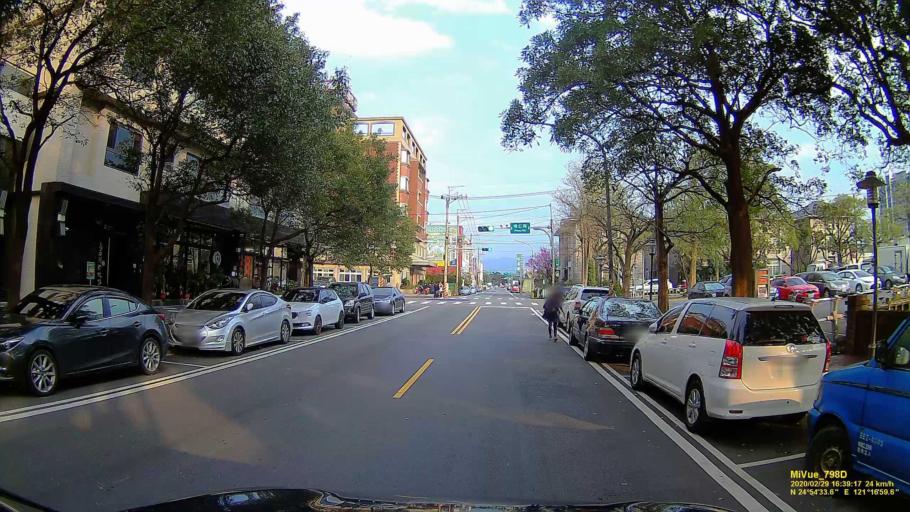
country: TW
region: Taiwan
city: Daxi
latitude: 24.9093
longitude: 121.2833
